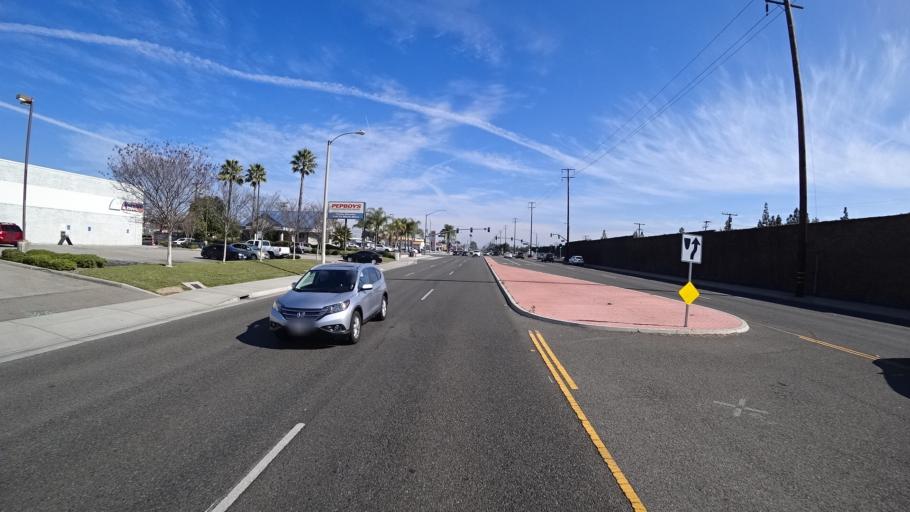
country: US
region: California
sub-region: Orange County
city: La Habra
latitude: 33.9174
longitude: -117.9473
